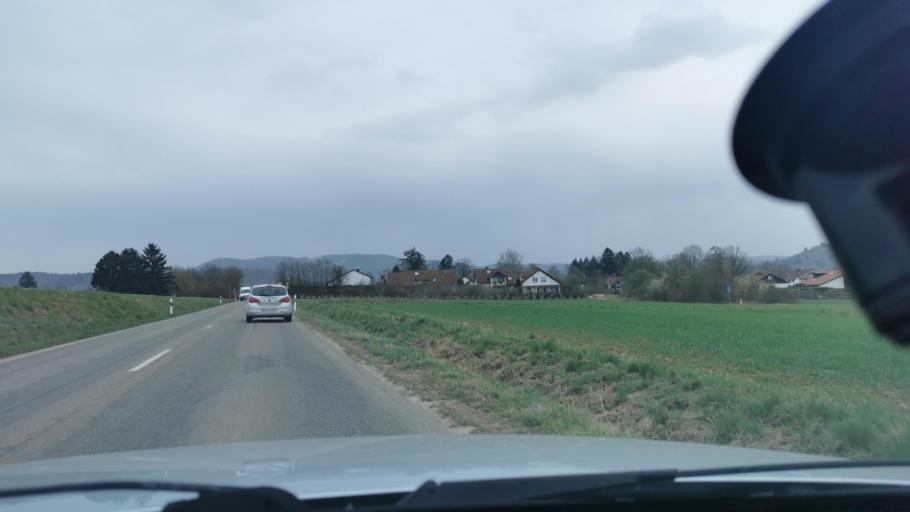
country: DE
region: Baden-Wuerttemberg
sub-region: Regierungsbezirk Stuttgart
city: Holzmaden
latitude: 48.6269
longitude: 9.5216
